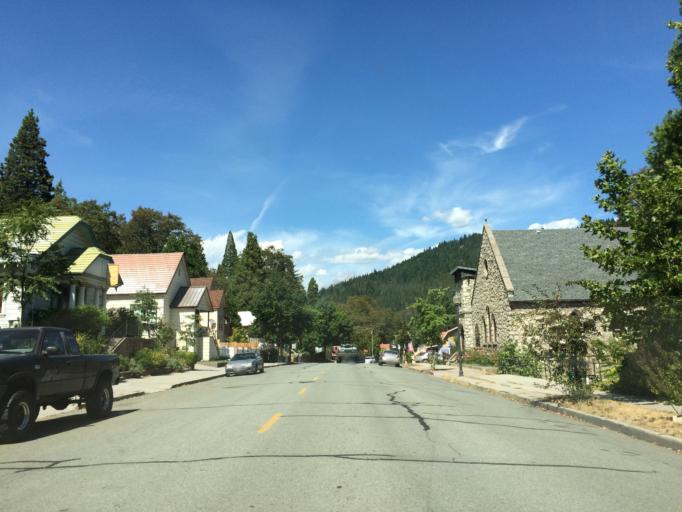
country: US
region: California
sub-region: Siskiyou County
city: Dunsmuir
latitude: 41.2082
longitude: -122.2734
